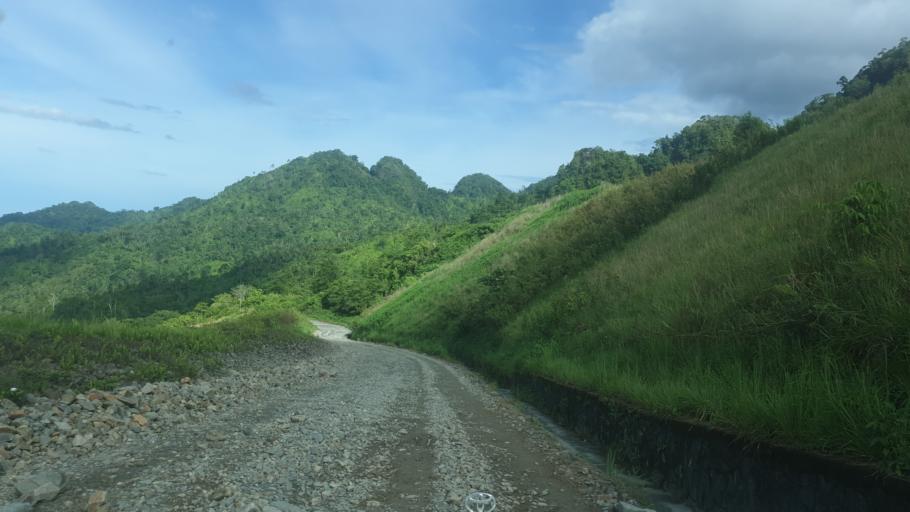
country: PG
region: Bougainville
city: Panguna
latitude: -6.3341
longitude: 155.4614
